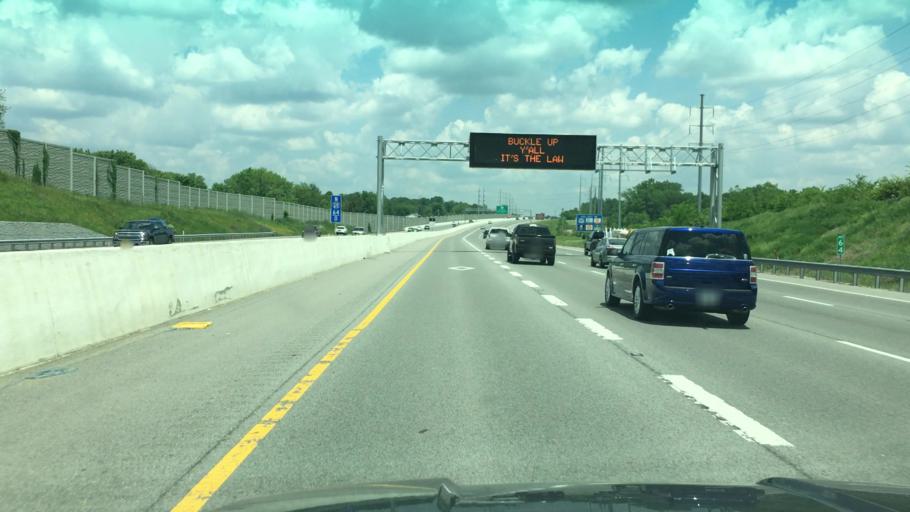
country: US
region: Tennessee
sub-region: Williamson County
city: Franklin
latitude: 35.8932
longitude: -86.8291
